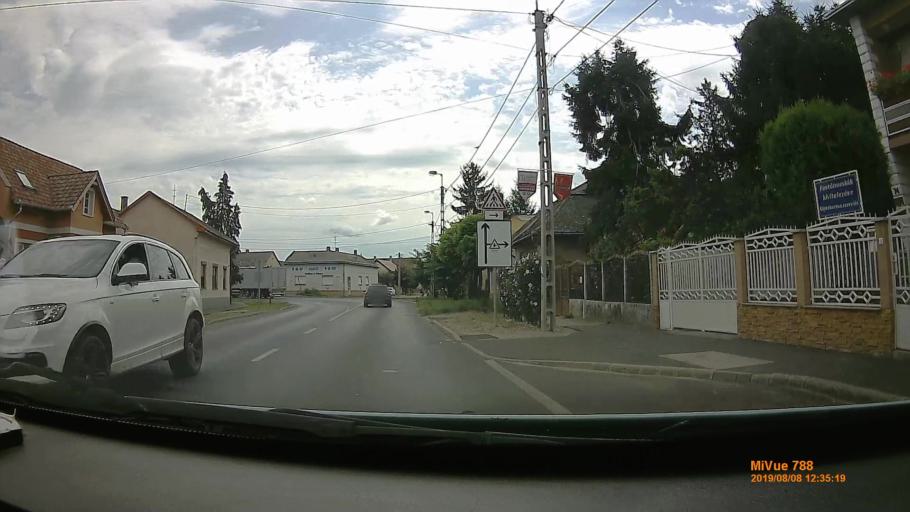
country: HU
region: Szabolcs-Szatmar-Bereg
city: Nyirbator
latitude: 47.8355
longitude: 22.1265
